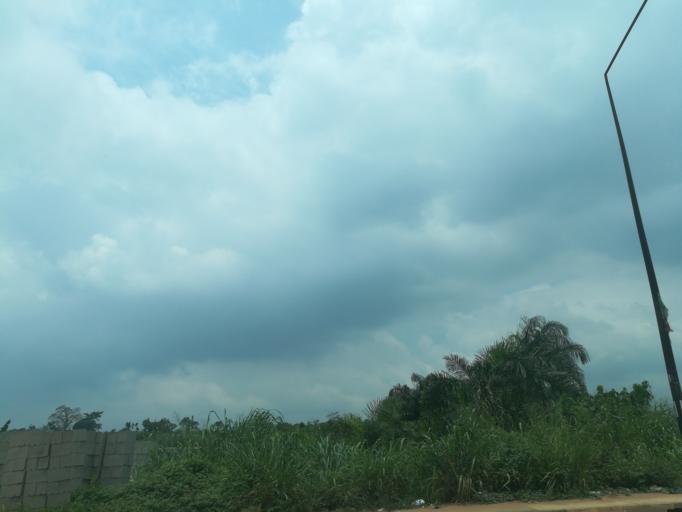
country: NG
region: Lagos
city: Ikorodu
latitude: 6.6246
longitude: 3.5258
